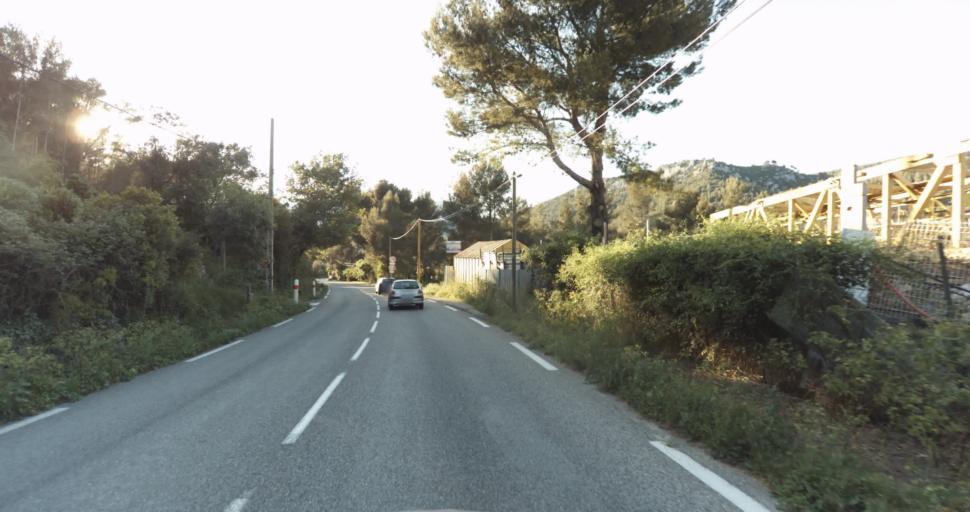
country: FR
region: Provence-Alpes-Cote d'Azur
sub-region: Departement du Var
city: Le Revest-les-Eaux
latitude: 43.1587
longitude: 5.9558
